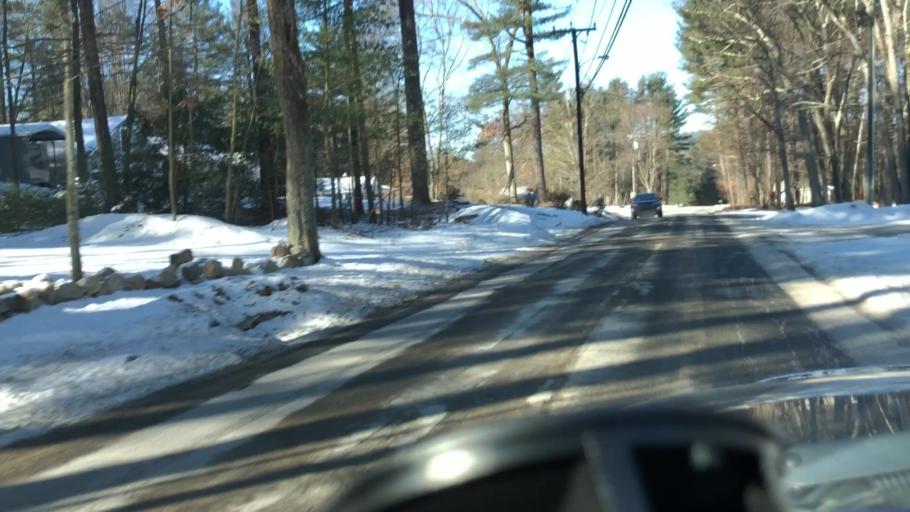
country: US
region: Massachusetts
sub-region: Hampshire County
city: Southampton
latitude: 42.2218
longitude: -72.7152
